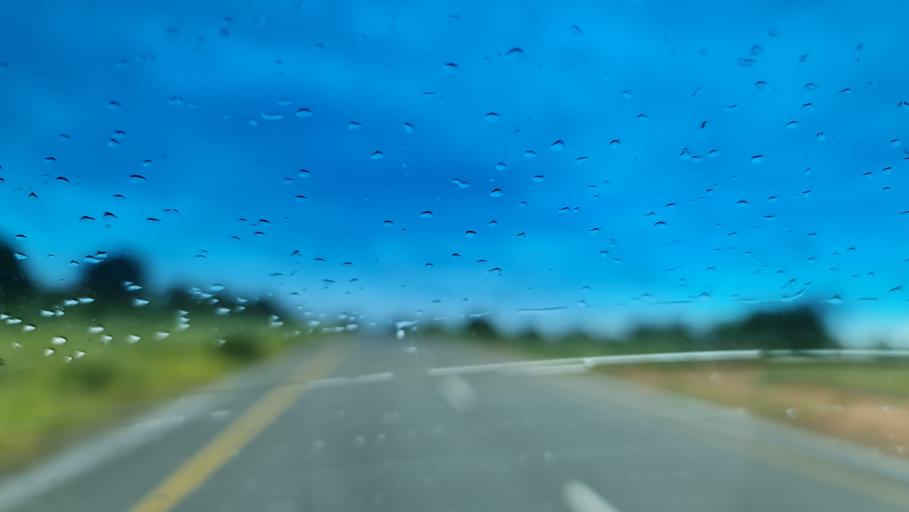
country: MZ
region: Nampula
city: Nampula
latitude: -15.5263
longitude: 39.3324
